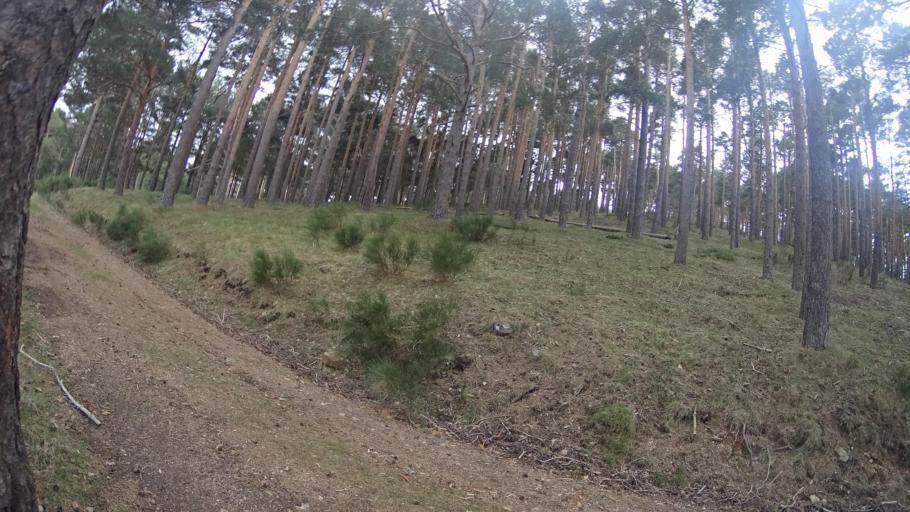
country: ES
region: Madrid
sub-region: Provincia de Madrid
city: Pinilla del Valle
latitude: 40.8690
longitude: -3.7946
